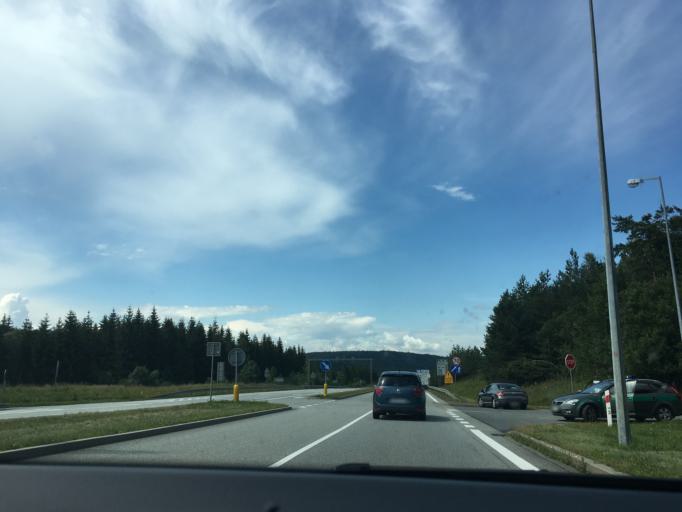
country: PL
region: Subcarpathian Voivodeship
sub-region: Powiat krosnienski
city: Jasliska
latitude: 49.4200
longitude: 21.6949
